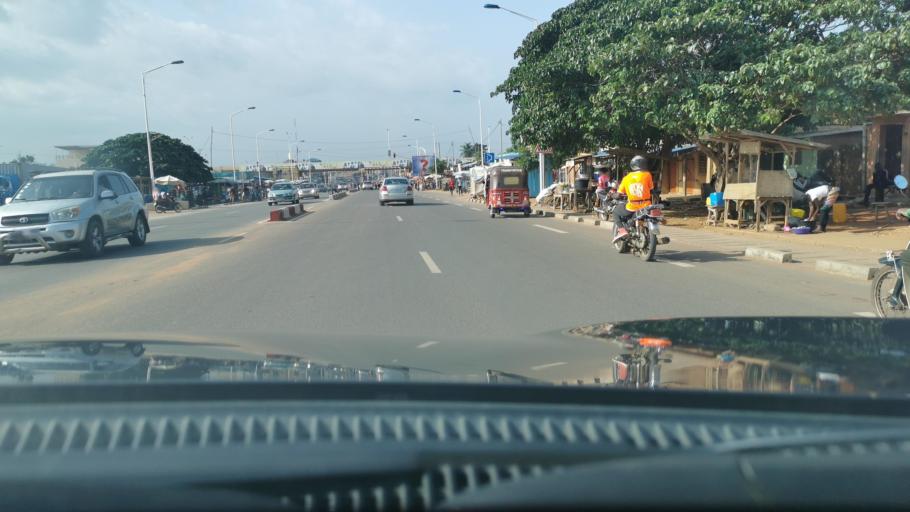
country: TG
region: Maritime
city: Lome
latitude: 6.2093
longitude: 1.2439
